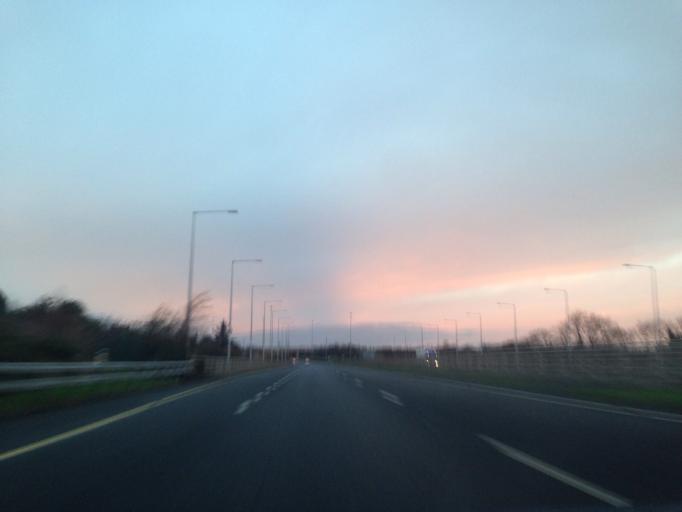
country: IE
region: Leinster
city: Loughlinstown
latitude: 53.2381
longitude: -6.1445
